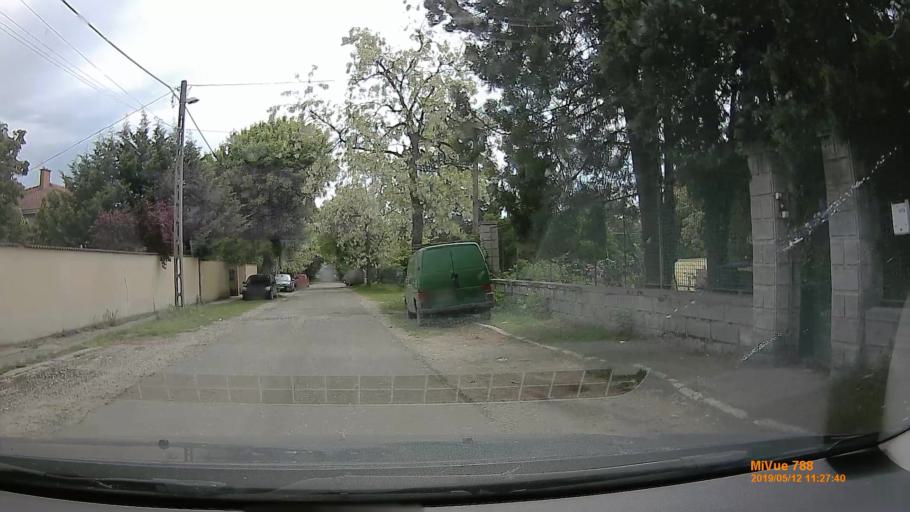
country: HU
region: Budapest
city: Budapest XVII. keruelet
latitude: 47.4652
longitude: 19.2452
